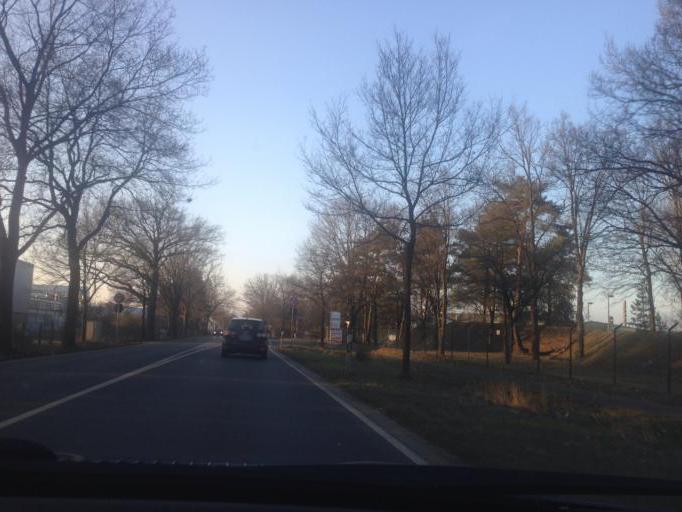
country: DE
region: Lower Saxony
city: Nienhagen
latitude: 52.5889
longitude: 10.1161
